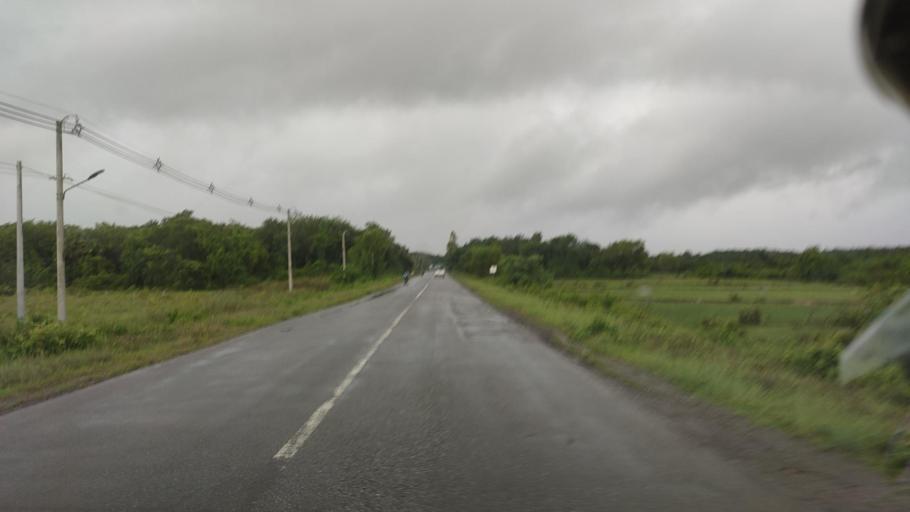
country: MM
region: Bago
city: Bago
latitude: 17.3635
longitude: 96.4586
